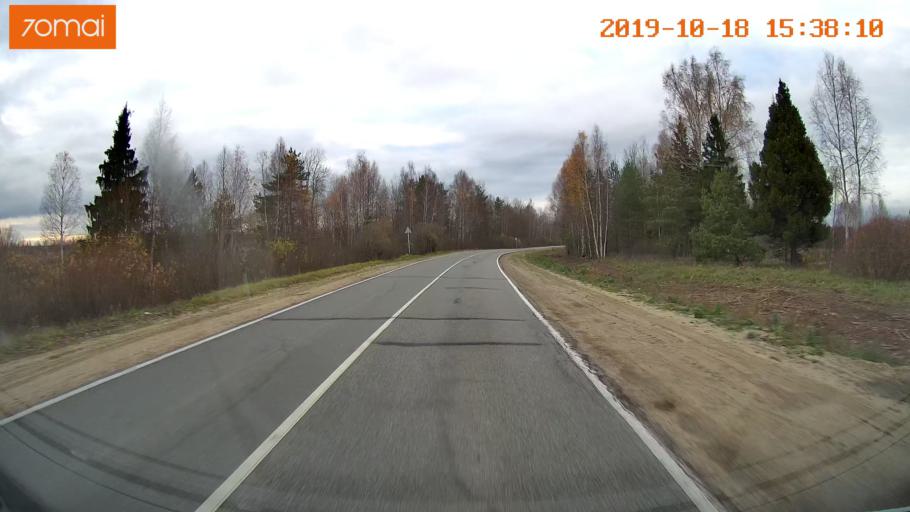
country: RU
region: Vladimir
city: Golovino
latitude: 55.9076
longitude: 40.6094
